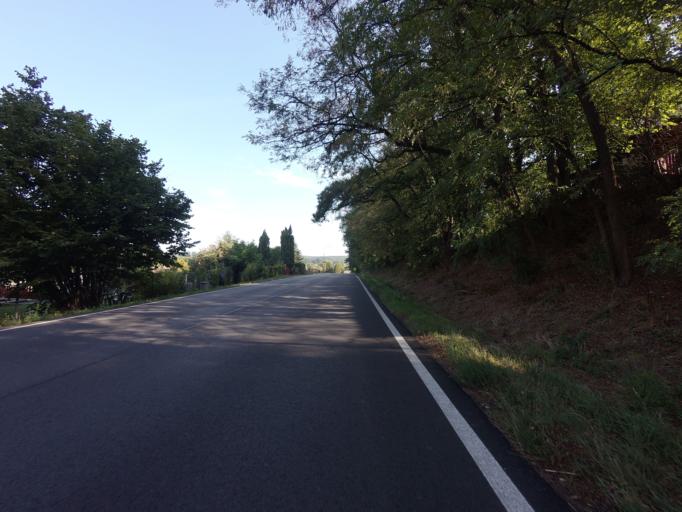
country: CZ
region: Jihocesky
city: Tyn nad Vltavou
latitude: 49.2495
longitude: 14.4212
